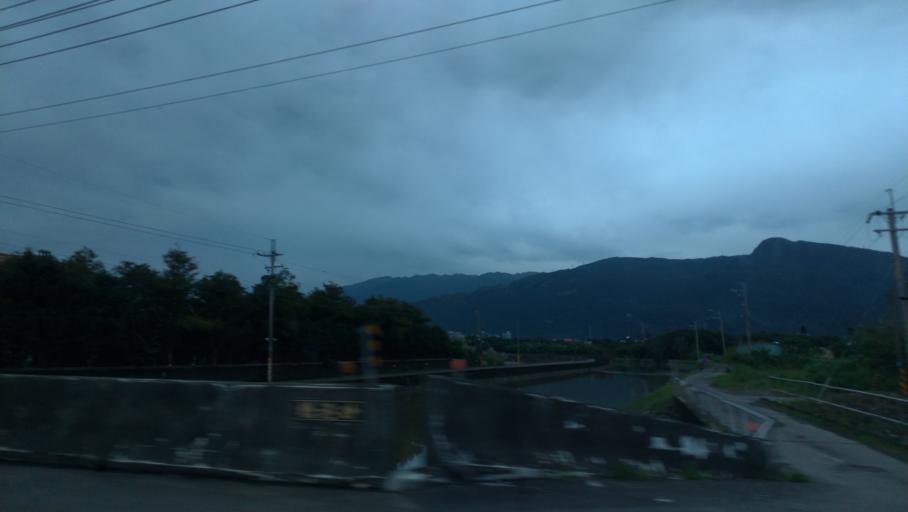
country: TW
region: Taiwan
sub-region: Yilan
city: Yilan
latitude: 24.8264
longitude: 121.8005
